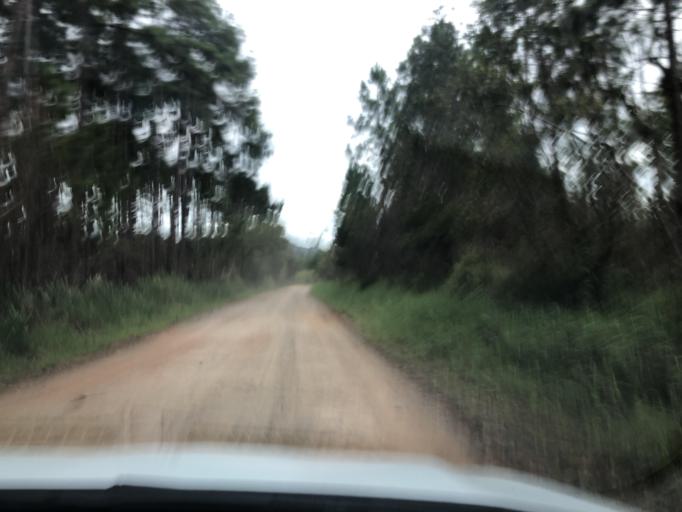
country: BR
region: Santa Catarina
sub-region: Florianopolis
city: Lagoa
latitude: -27.5469
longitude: -48.4432
